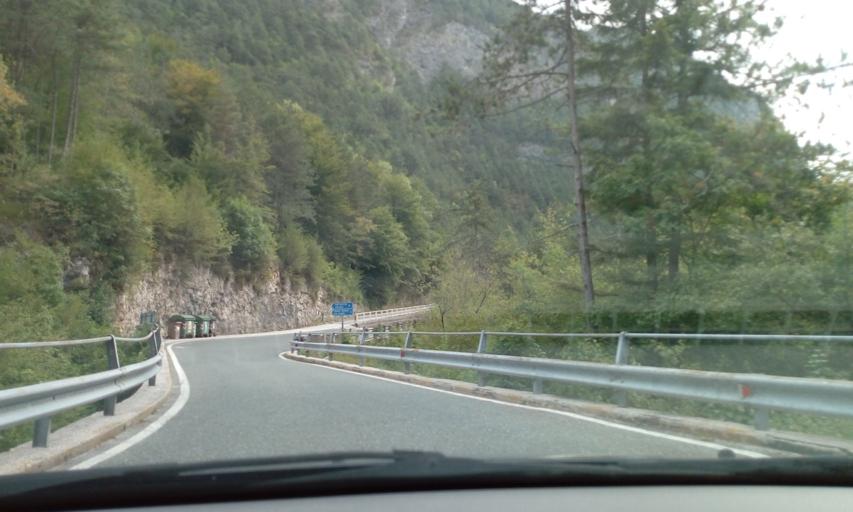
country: IT
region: Friuli Venezia Giulia
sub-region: Provincia di Udine
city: Chiusaforte
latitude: 46.3959
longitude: 13.3322
